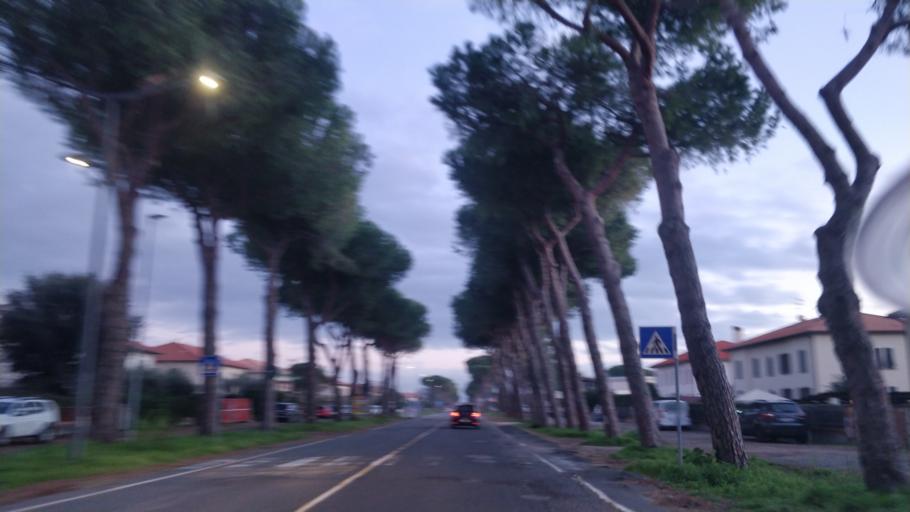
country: IT
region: Tuscany
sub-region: Provincia di Livorno
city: Rosignano Solvay-Castiglioncello
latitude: 43.3862
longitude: 10.4360
